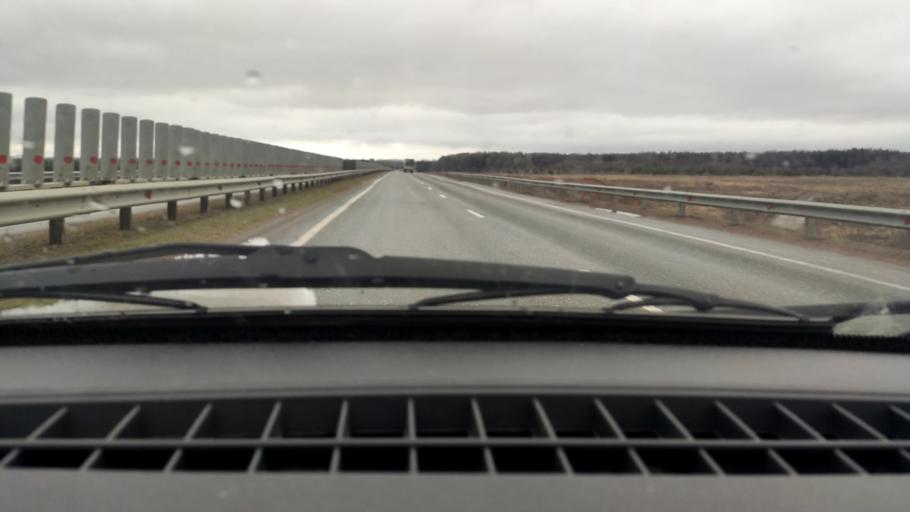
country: RU
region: Bashkortostan
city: Kushnarenkovo
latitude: 55.0611
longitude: 55.3917
